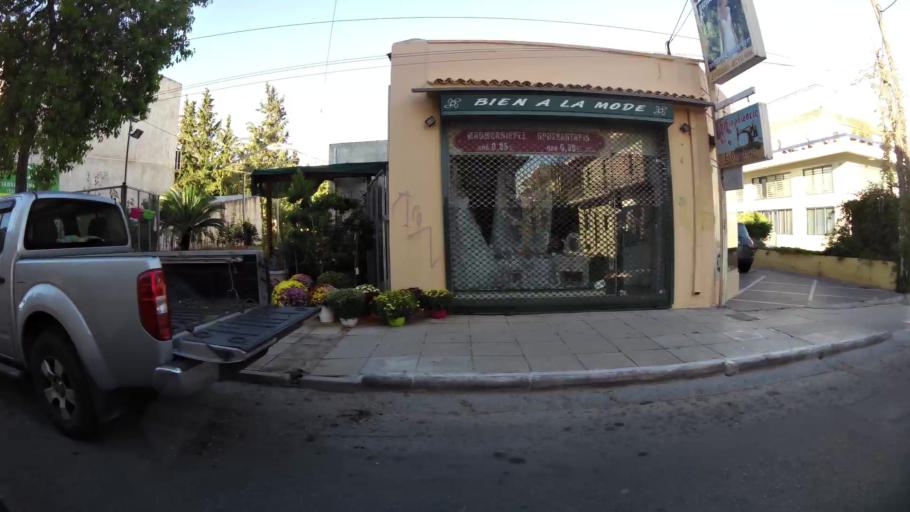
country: GR
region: Attica
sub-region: Nomarchia Anatolikis Attikis
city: Koropi
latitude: 37.9044
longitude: 23.8726
